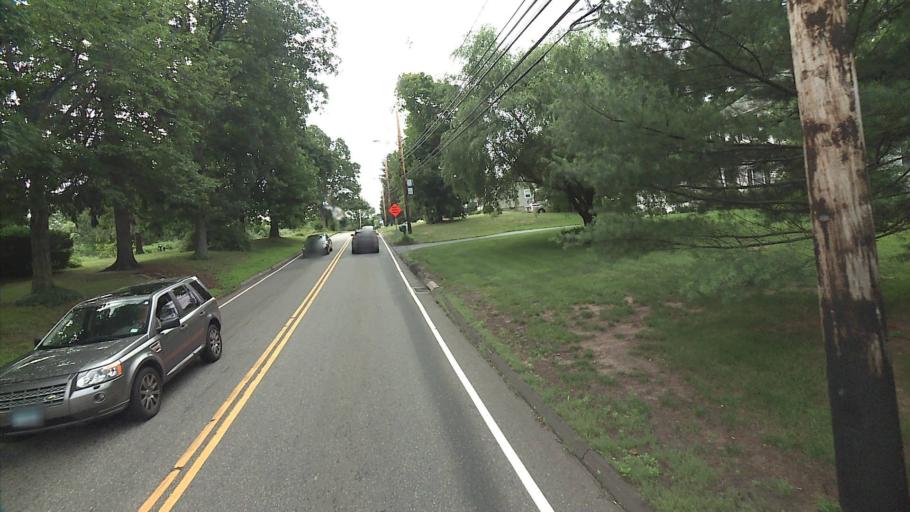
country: US
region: Connecticut
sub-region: New Haven County
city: Wallingford Center
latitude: 41.4365
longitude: -72.8041
